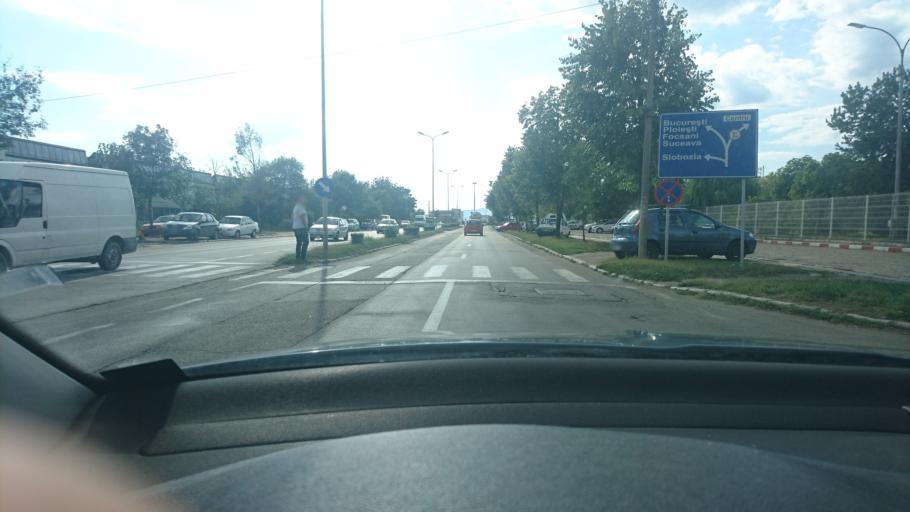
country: RO
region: Buzau
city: Buzau
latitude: 45.1339
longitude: 26.8194
